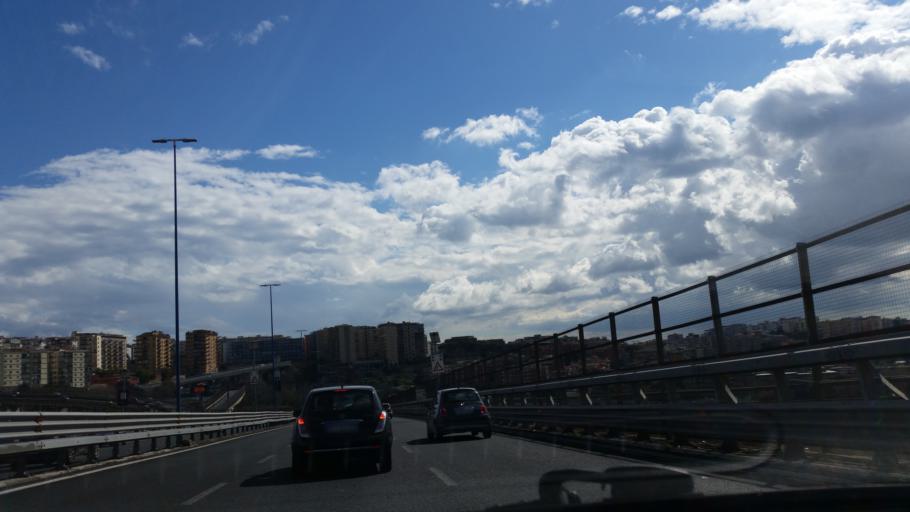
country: IT
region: Campania
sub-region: Provincia di Napoli
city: Napoli
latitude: 40.8484
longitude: 14.2152
